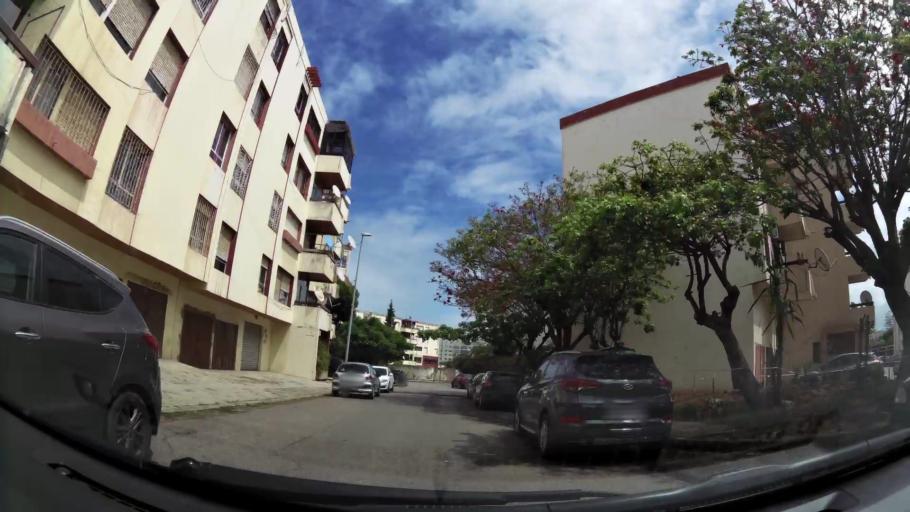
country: MA
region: Grand Casablanca
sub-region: Casablanca
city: Casablanca
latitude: 33.5681
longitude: -7.6321
